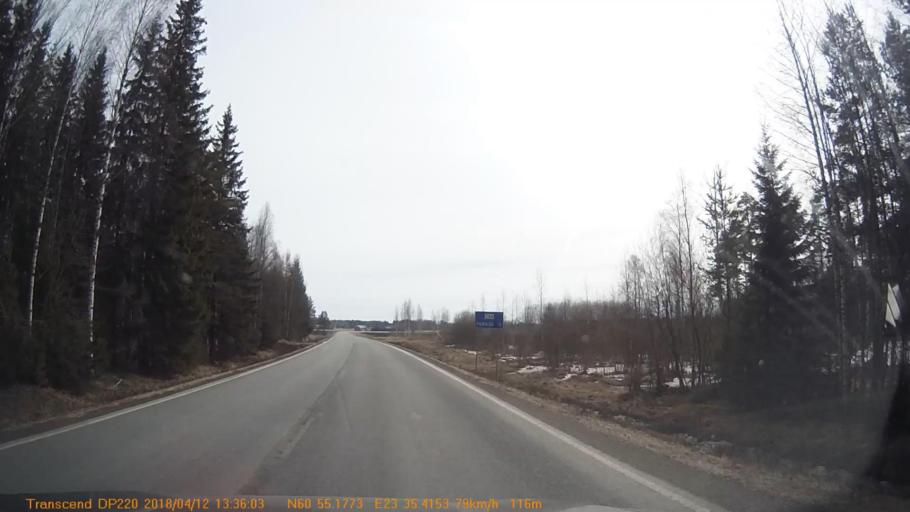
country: FI
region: Haeme
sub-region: Forssa
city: Forssa
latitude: 60.9193
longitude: 23.5905
